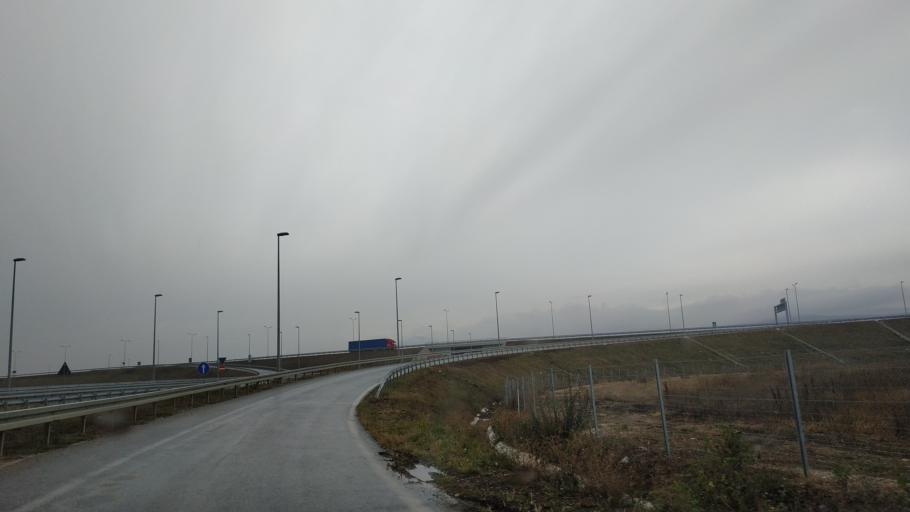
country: RS
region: Central Serbia
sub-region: Pirotski Okrug
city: Pirot
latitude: 43.1224
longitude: 22.6197
